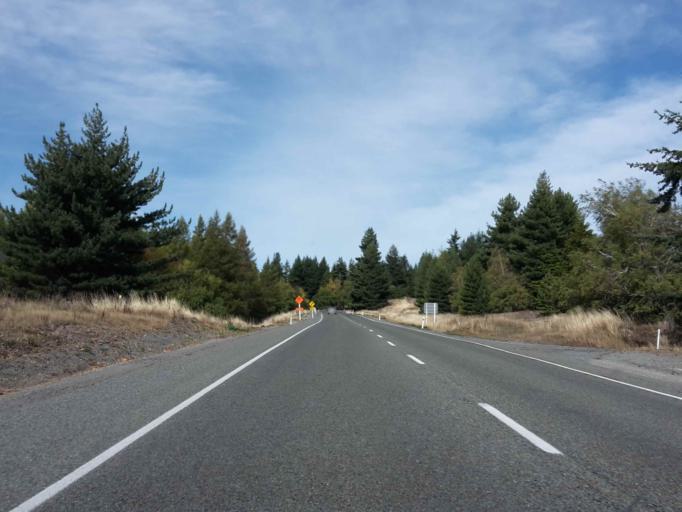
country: NZ
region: Canterbury
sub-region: Timaru District
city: Pleasant Point
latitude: -44.0101
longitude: 170.4978
